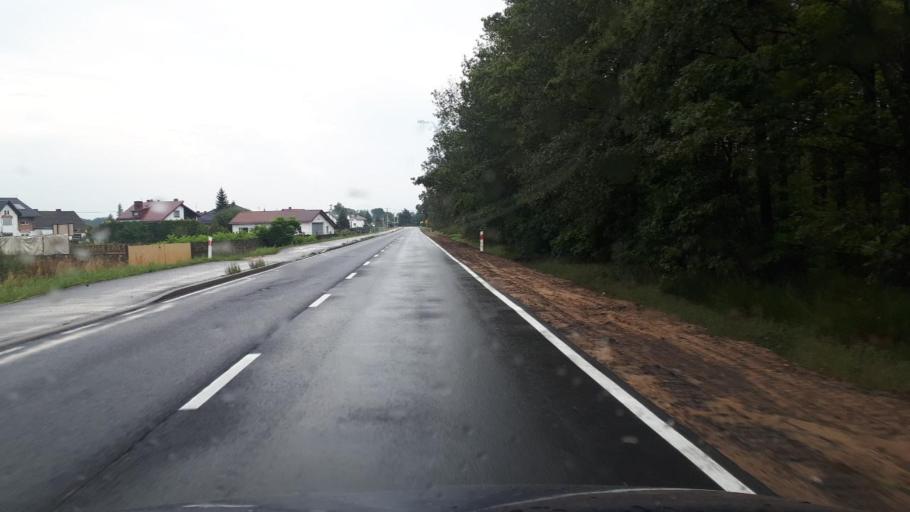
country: PL
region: Silesian Voivodeship
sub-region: Powiat lubliniecki
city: Sierakow Slaski
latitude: 50.8051
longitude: 18.5622
